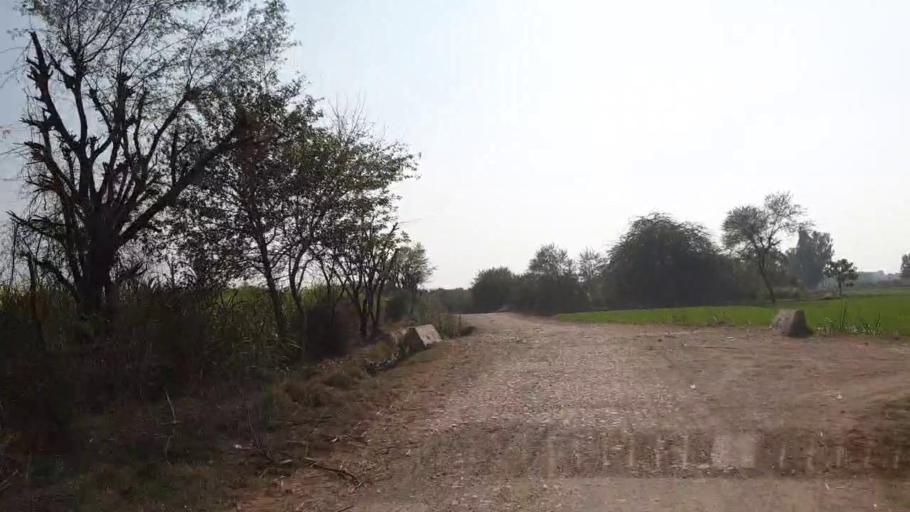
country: PK
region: Sindh
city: Tando Adam
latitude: 25.6788
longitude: 68.5660
